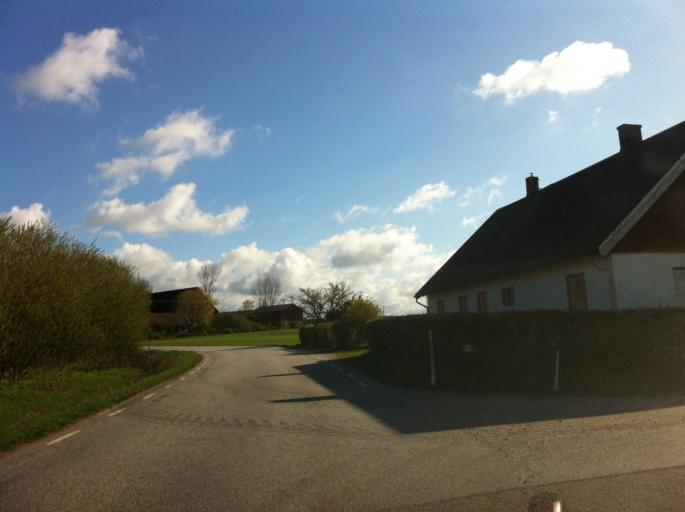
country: SE
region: Skane
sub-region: Eslovs Kommun
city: Eslov
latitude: 55.8746
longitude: 13.2455
